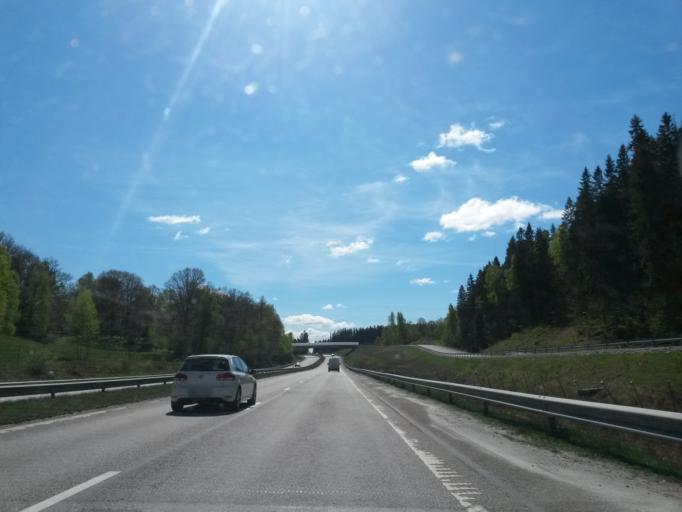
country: SE
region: Vaestra Goetaland
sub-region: Alingsas Kommun
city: Ingared
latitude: 57.8884
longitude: 12.4886
